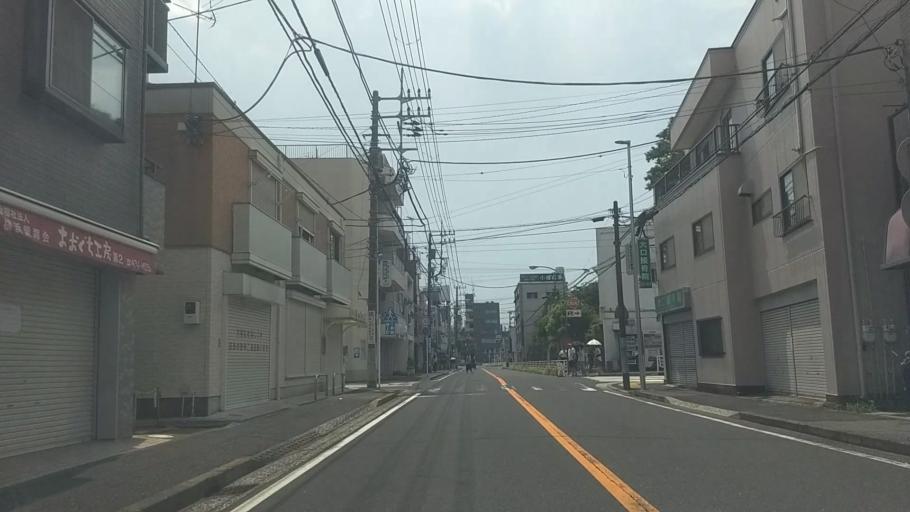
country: JP
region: Kanagawa
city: Yokohama
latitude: 35.4939
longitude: 139.6454
